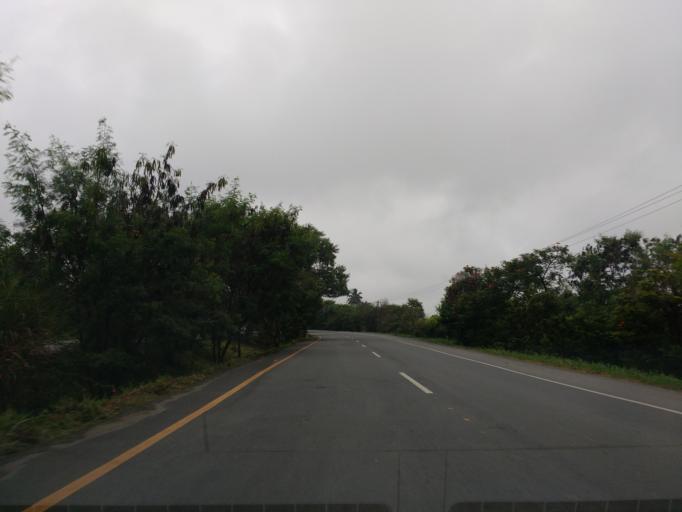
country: CO
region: Valle del Cauca
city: Palmira
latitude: 3.5678
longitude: -76.3320
